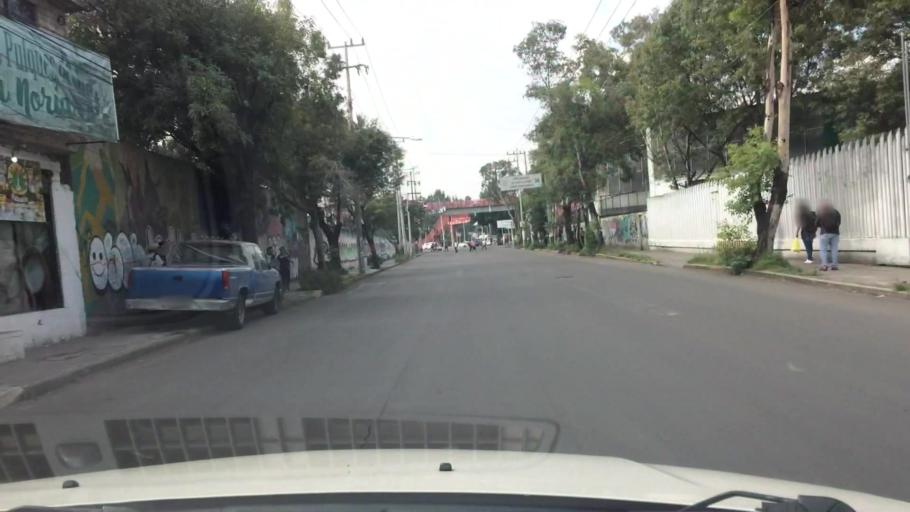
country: MX
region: Mexico City
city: Xochimilco
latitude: 19.2671
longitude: -99.1269
